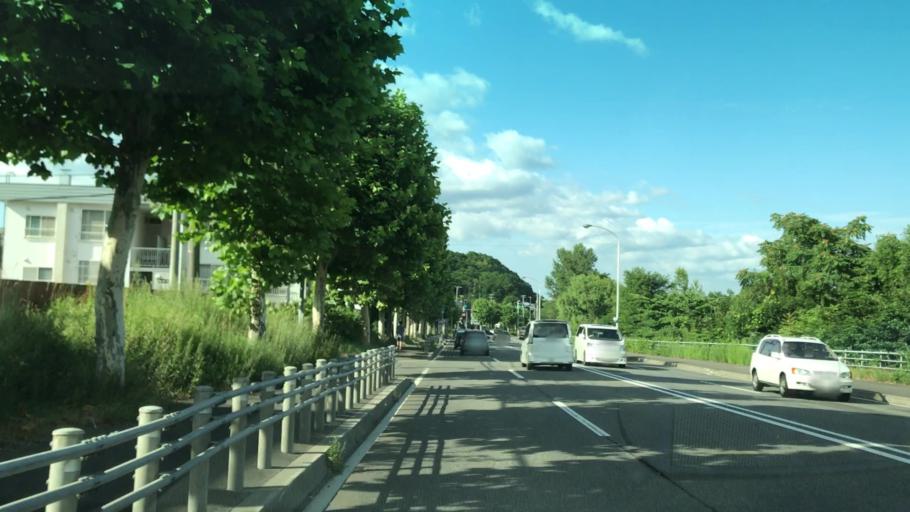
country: JP
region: Hokkaido
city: Sapporo
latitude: 42.9844
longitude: 141.3476
